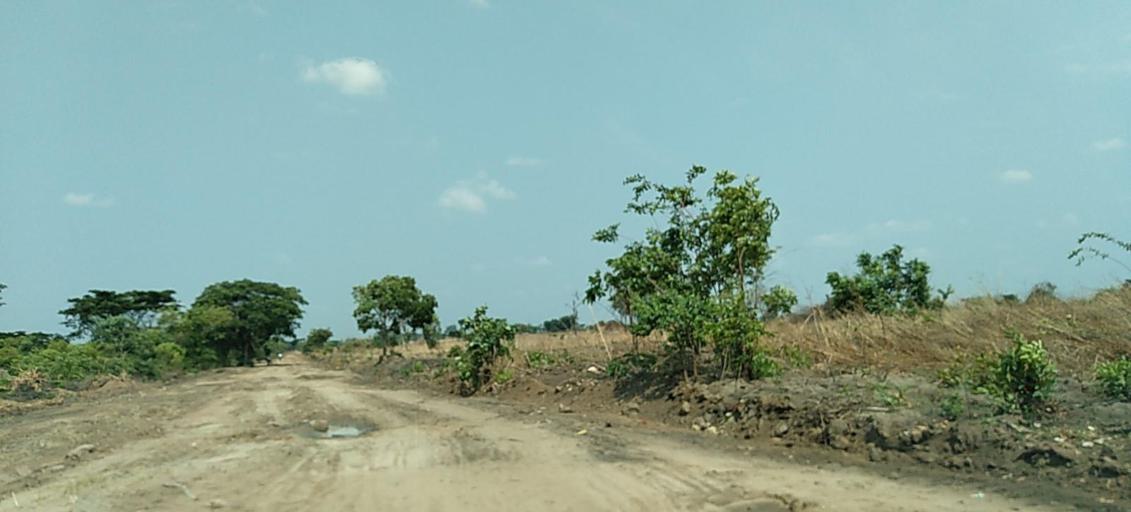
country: ZM
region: Copperbelt
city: Luanshya
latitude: -13.0898
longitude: 28.2695
